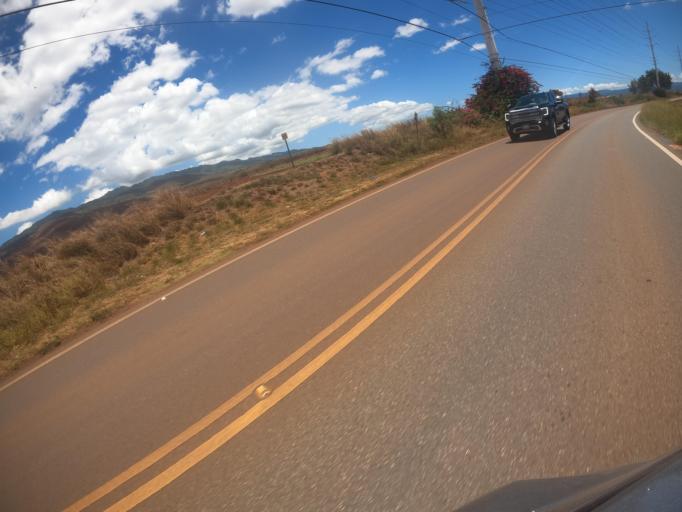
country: US
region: Hawaii
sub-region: Honolulu County
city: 'Ewa Villages
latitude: 21.3668
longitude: -158.0522
